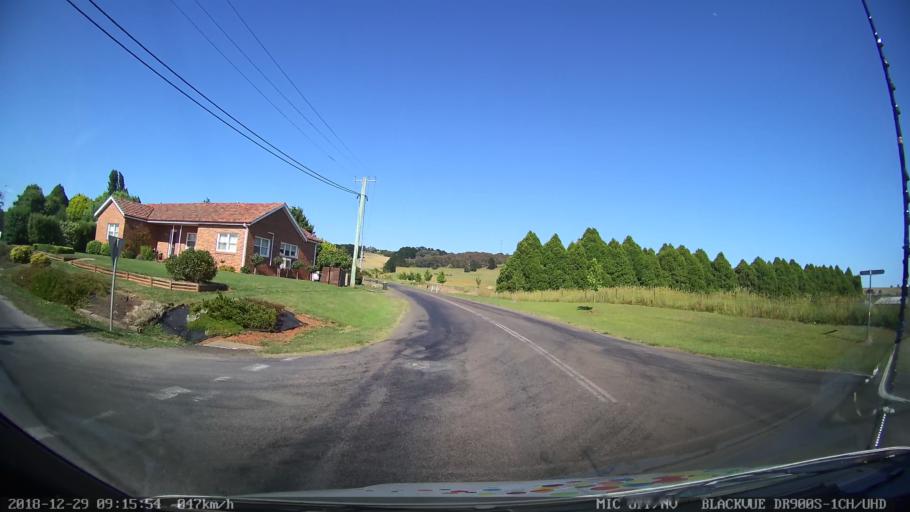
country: AU
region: New South Wales
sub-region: Upper Lachlan Shire
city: Crookwell
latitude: -34.4558
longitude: 149.4562
